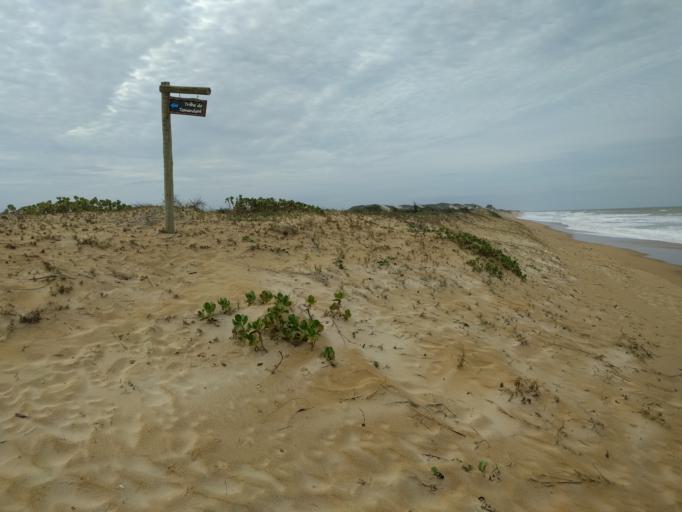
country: BR
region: Espirito Santo
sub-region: Conceicao Da Barra
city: Conceicao da Barra
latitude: -18.4197
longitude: -39.6999
